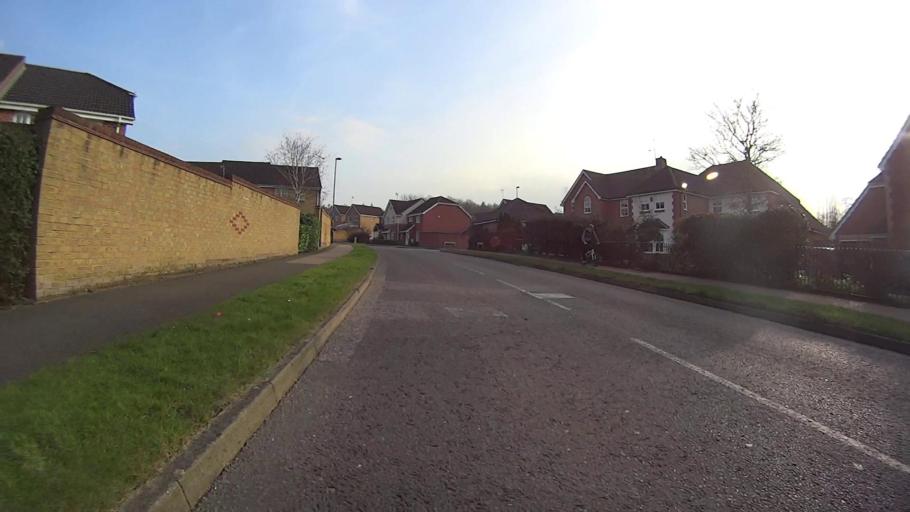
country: GB
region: England
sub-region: West Sussex
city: Maidenbower
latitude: 51.1025
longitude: -0.1501
